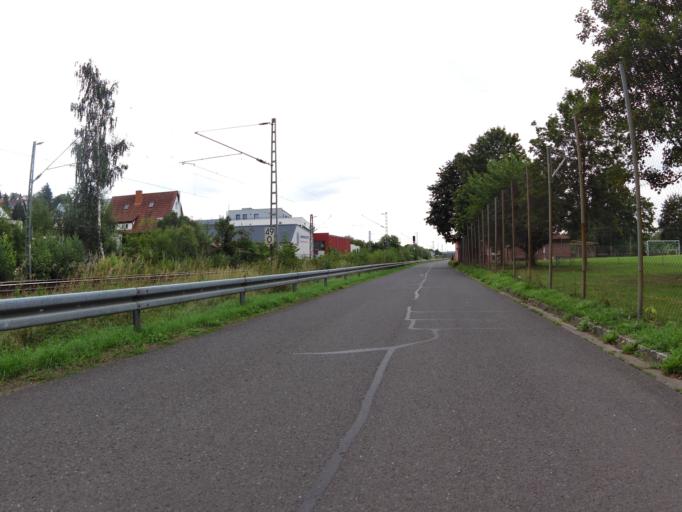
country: DE
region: Bavaria
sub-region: Regierungsbezirk Unterfranken
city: Schonungen
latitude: 50.0470
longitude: 10.3073
